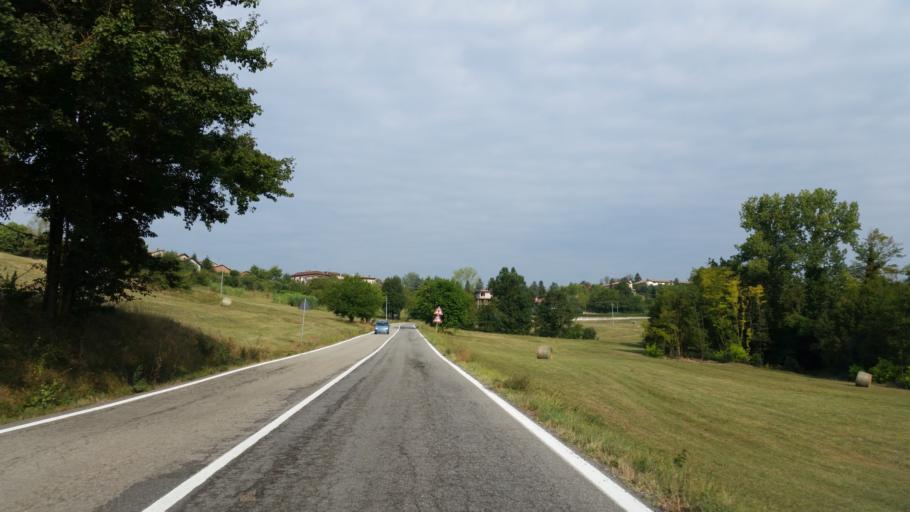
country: IT
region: Piedmont
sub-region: Provincia di Asti
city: Montiglio
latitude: 45.0772
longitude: 8.0824
